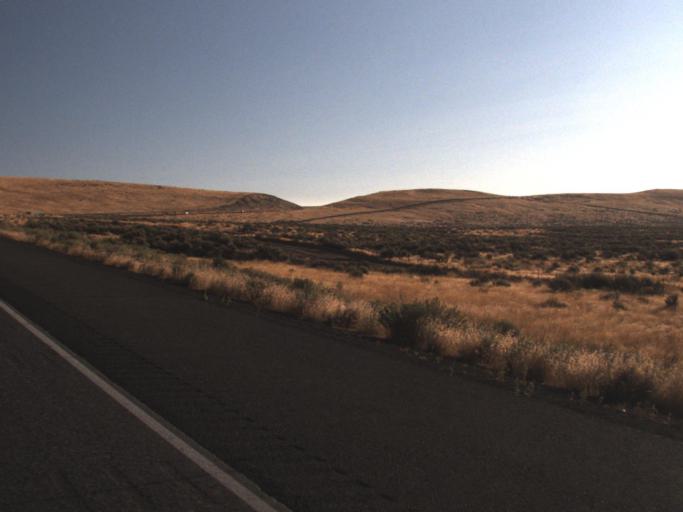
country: US
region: Washington
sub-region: Yakima County
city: Terrace Heights
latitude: 46.7171
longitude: -120.4099
